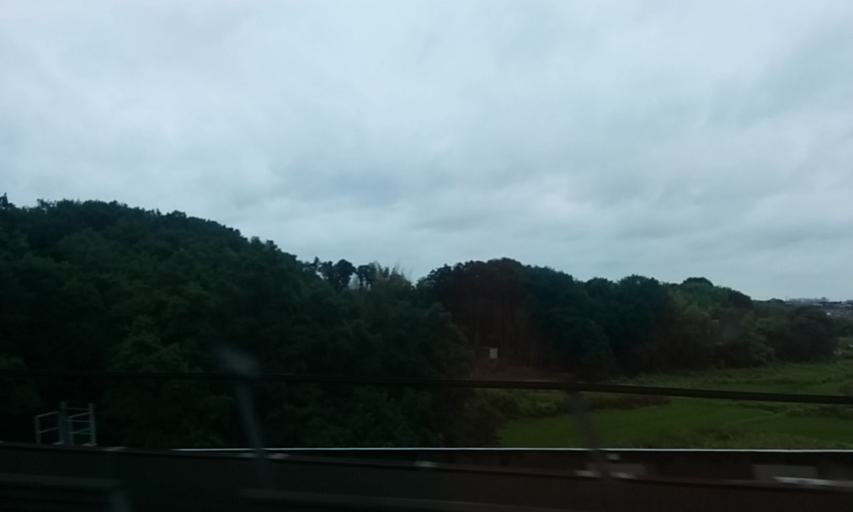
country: JP
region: Saitama
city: Ageoshimo
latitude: 35.9757
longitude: 139.6246
